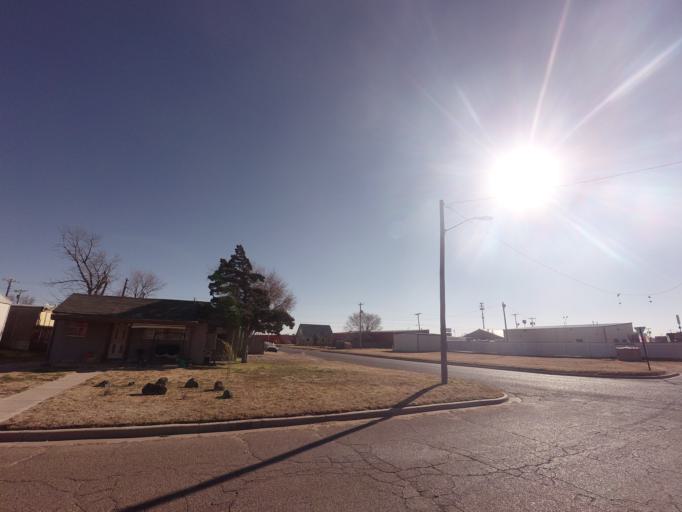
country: US
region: New Mexico
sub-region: Curry County
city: Clovis
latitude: 34.3999
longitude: -103.1927
